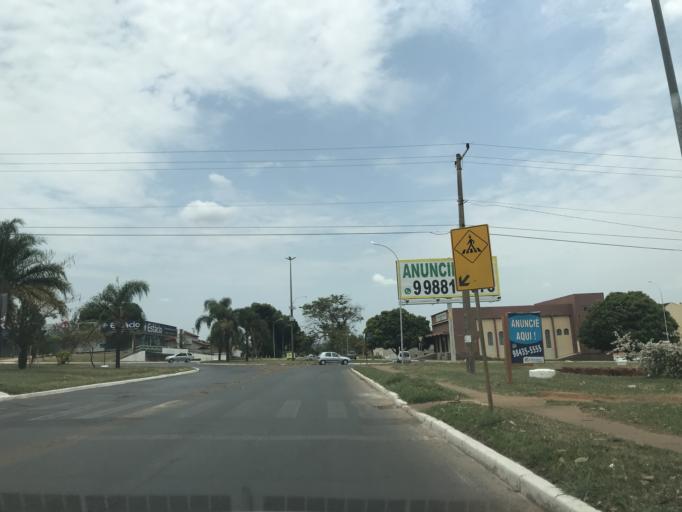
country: BR
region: Federal District
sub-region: Brasilia
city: Brasilia
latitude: -15.6512
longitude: -47.8040
